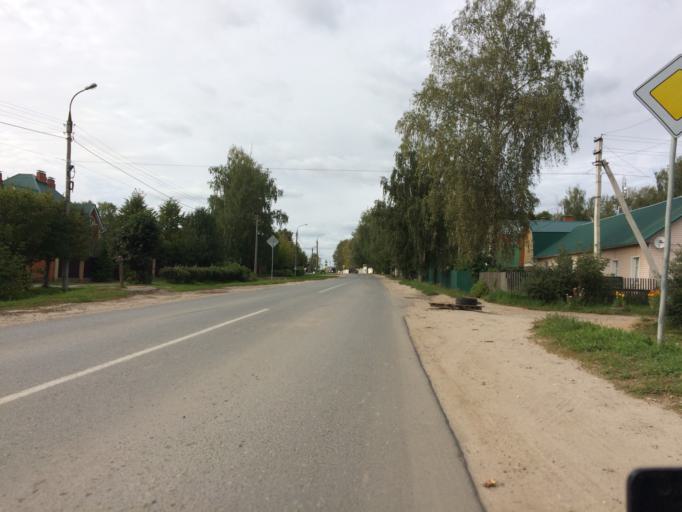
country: RU
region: Mariy-El
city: Yoshkar-Ola
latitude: 56.6518
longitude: 47.9793
